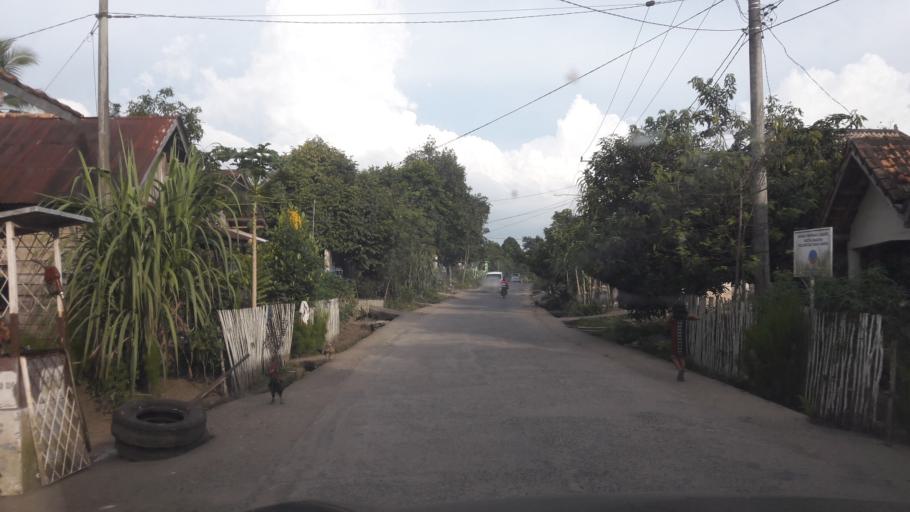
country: ID
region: South Sumatra
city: Gunungmenang
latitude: -3.2902
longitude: 104.0840
